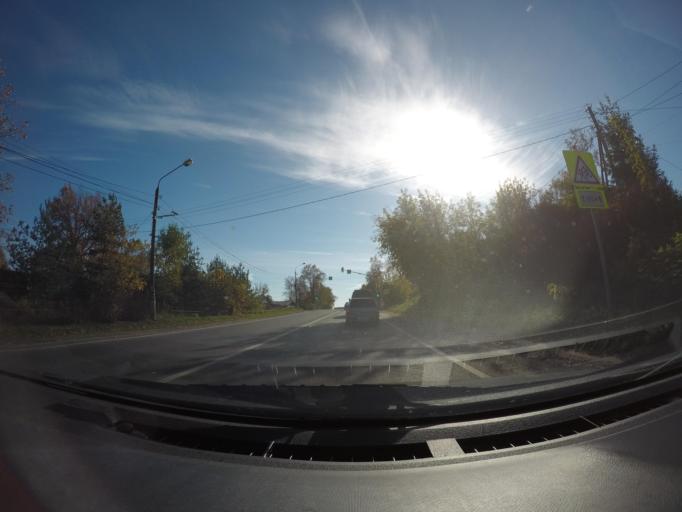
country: RU
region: Moskovskaya
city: Tomilino
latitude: 55.6307
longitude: 37.9464
